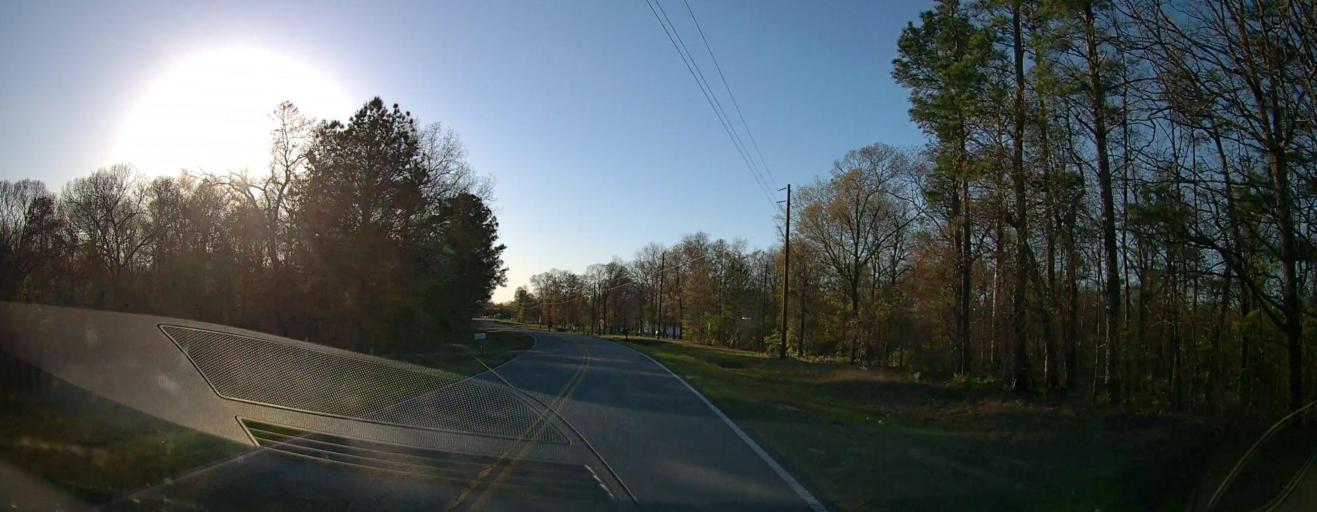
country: US
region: Georgia
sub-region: Wilkinson County
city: Gordon
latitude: 32.8819
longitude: -83.2802
